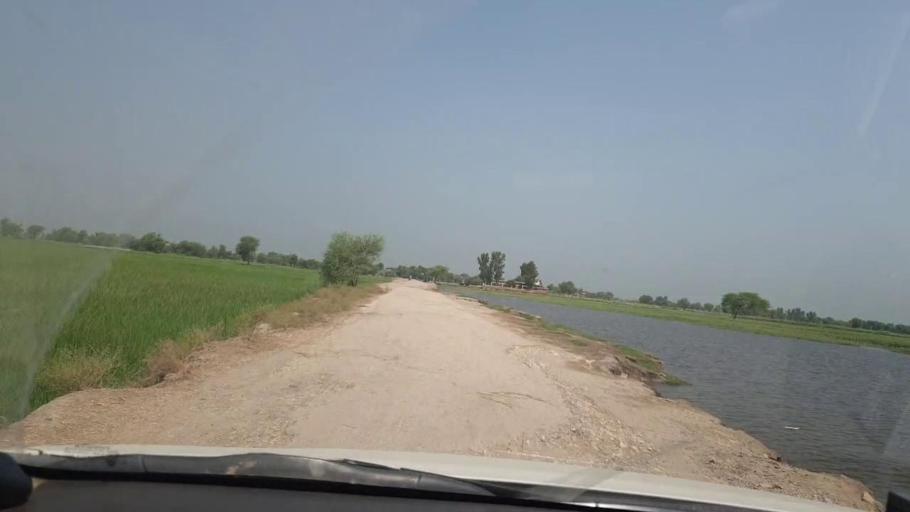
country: PK
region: Sindh
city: Chak
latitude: 27.8758
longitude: 68.7844
